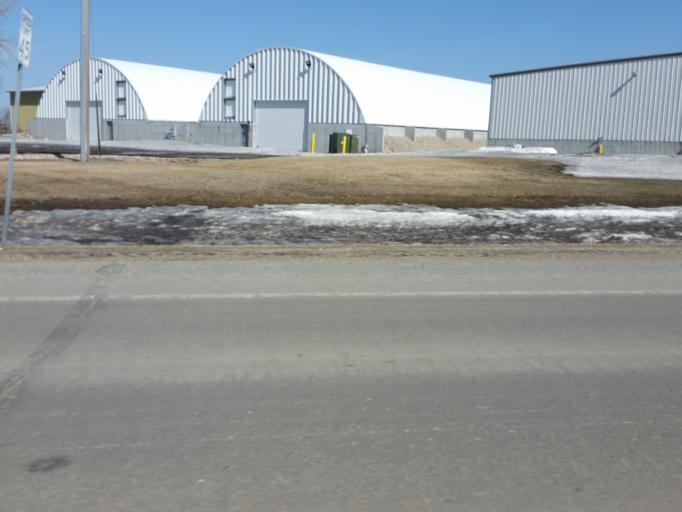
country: US
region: North Dakota
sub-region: Walsh County
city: Grafton
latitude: 48.2964
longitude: -97.3733
